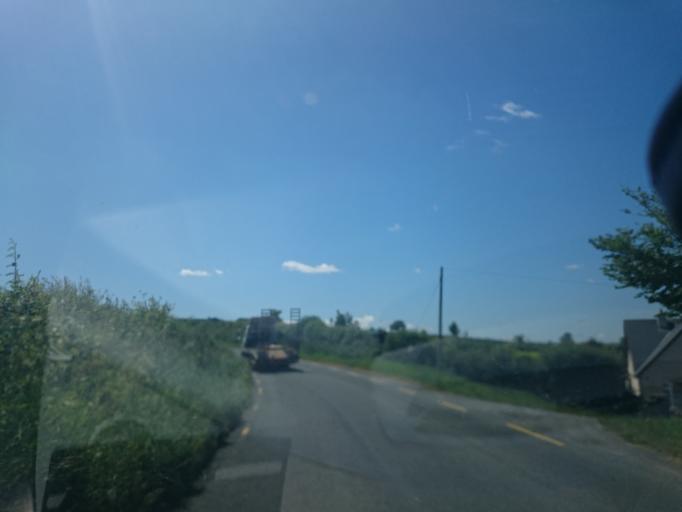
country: IE
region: Leinster
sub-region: Kilkenny
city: Graiguenamanagh
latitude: 52.6099
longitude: -6.9934
